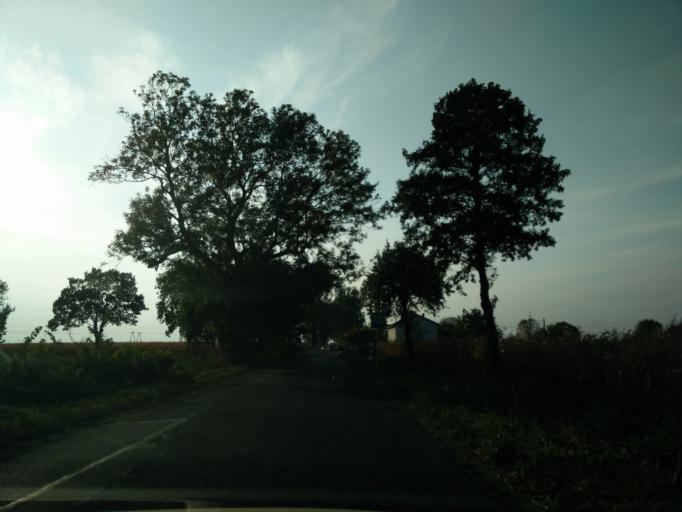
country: PL
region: Greater Poland Voivodeship
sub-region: Powiat sredzki
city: Sroda Wielkopolska
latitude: 52.1878
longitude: 17.2891
